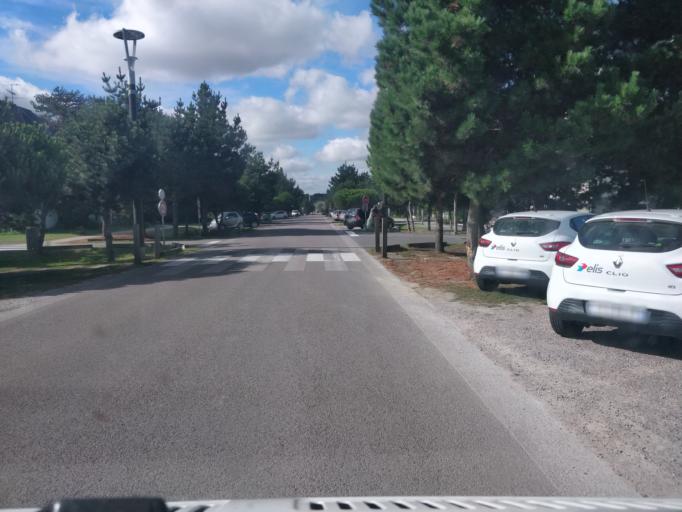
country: FR
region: Brittany
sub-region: Departement des Cotes-d'Armor
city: Plurien
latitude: 48.6387
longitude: -2.4055
